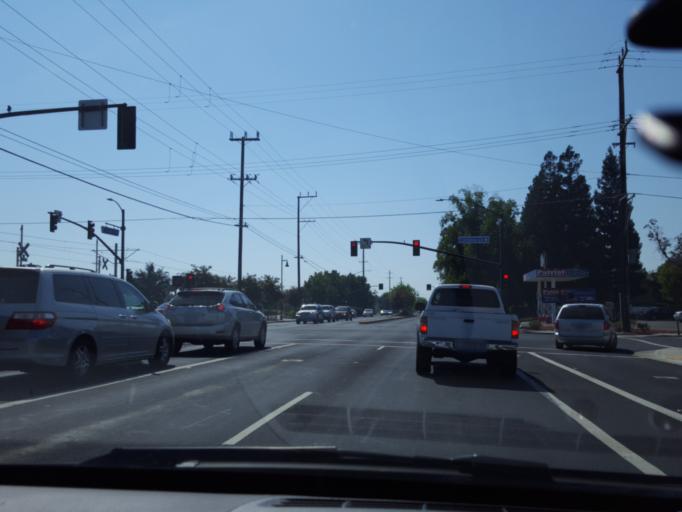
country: US
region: California
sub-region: Sacramento County
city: Rancho Cordova
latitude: 38.5996
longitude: -121.2819
